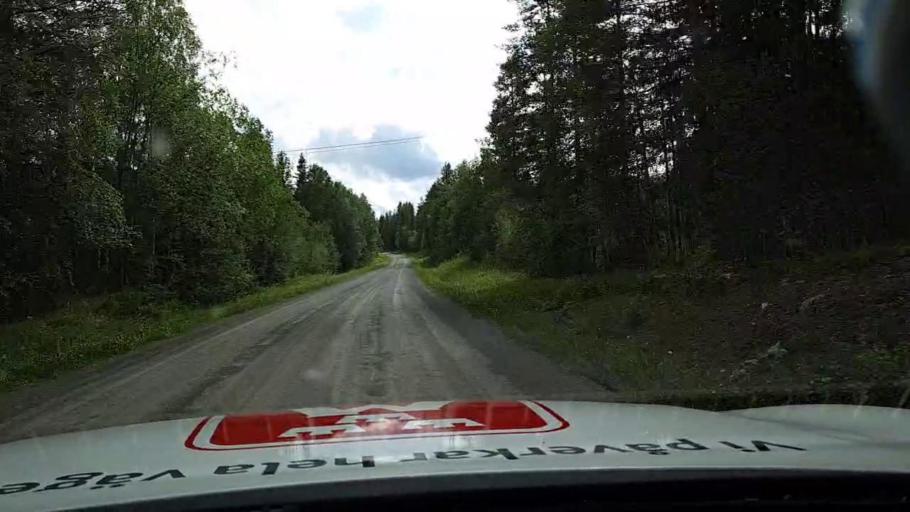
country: SE
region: Jaemtland
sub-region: OEstersunds Kommun
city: Brunflo
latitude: 63.1188
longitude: 15.0897
